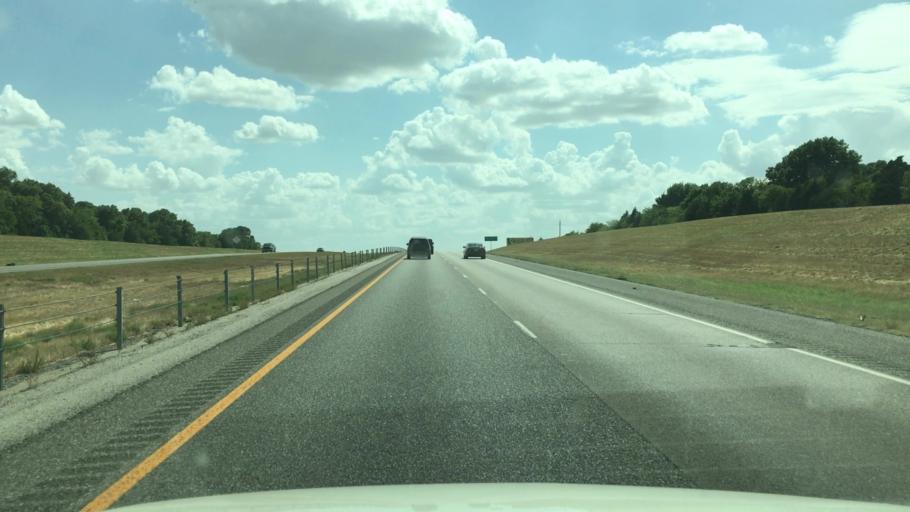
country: US
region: Texas
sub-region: Ellis County
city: Plum Grove
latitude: 32.0933
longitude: -97.0280
